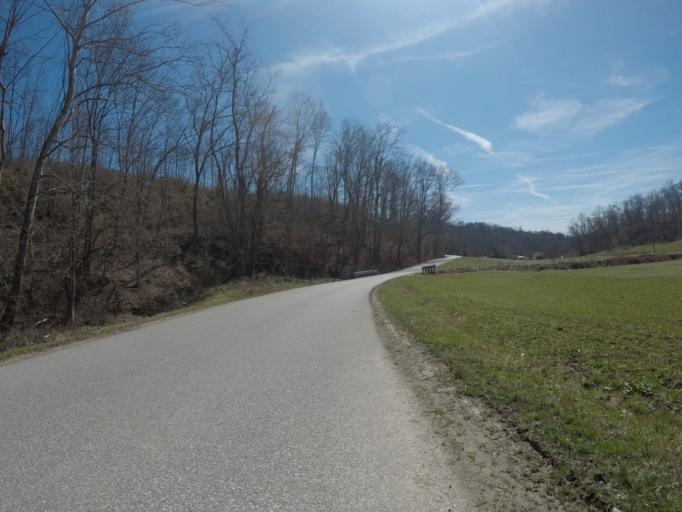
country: US
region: Ohio
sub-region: Lawrence County
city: South Point
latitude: 38.4768
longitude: -82.5660
